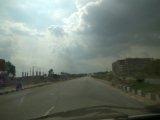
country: IN
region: Karnataka
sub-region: Kolar
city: Malur
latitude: 13.1296
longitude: 77.9905
